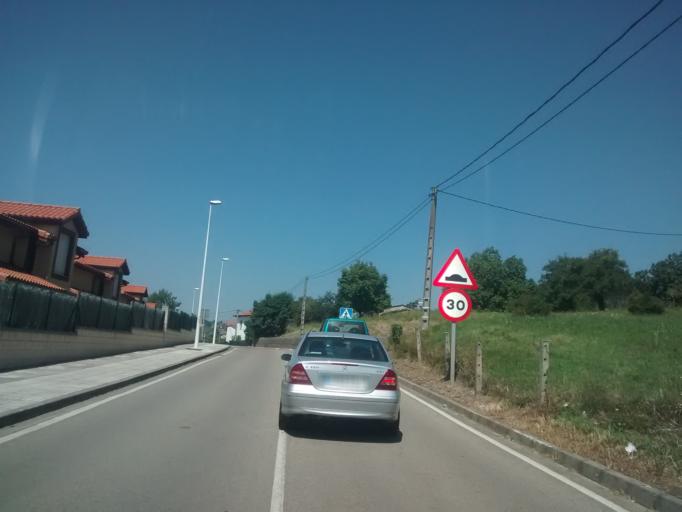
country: ES
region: Cantabria
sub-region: Provincia de Cantabria
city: San Miguel de Meruelo
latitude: 43.4583
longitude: -3.5807
